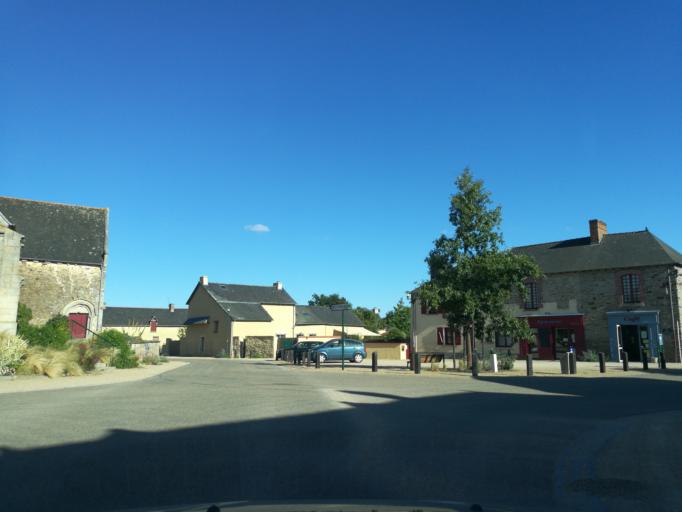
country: FR
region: Brittany
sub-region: Departement d'Ille-et-Vilaine
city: Montauban-de-Bretagne
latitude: 48.1730
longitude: -2.0292
